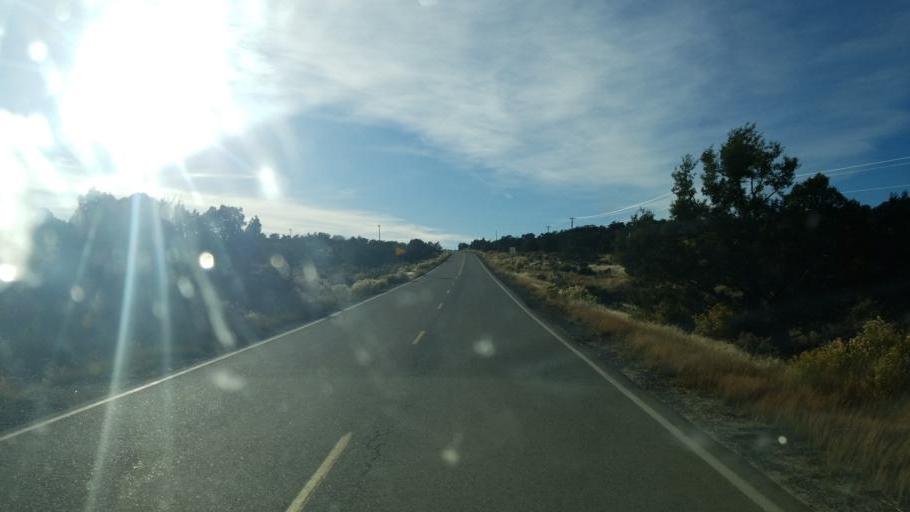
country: US
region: New Mexico
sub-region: San Juan County
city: Bloomfield
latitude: 36.7334
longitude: -107.6362
